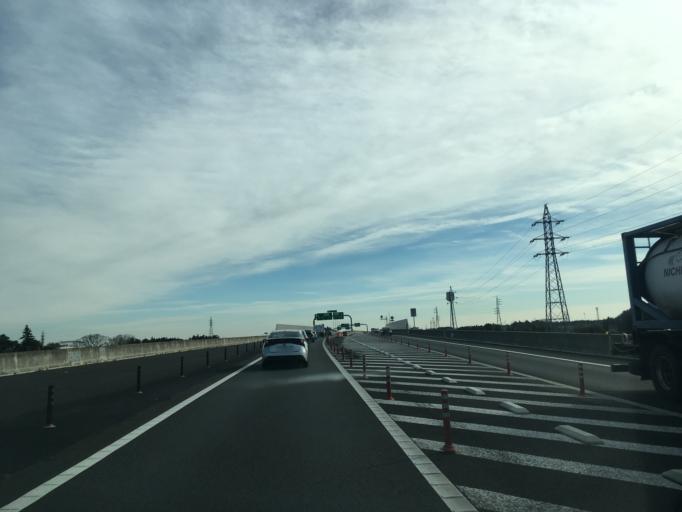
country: JP
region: Ibaraki
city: Naka
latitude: 36.0357
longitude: 140.1200
